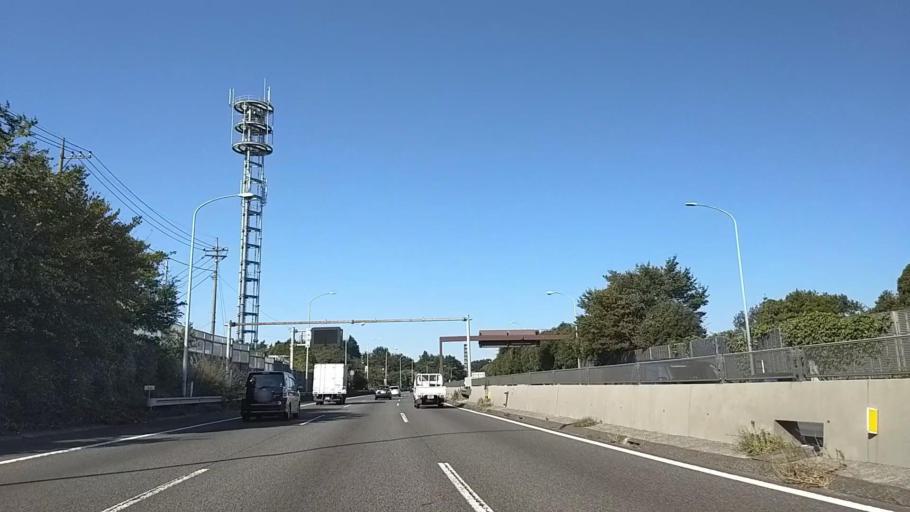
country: JP
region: Kanagawa
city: Yokohama
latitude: 35.4538
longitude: 139.5554
